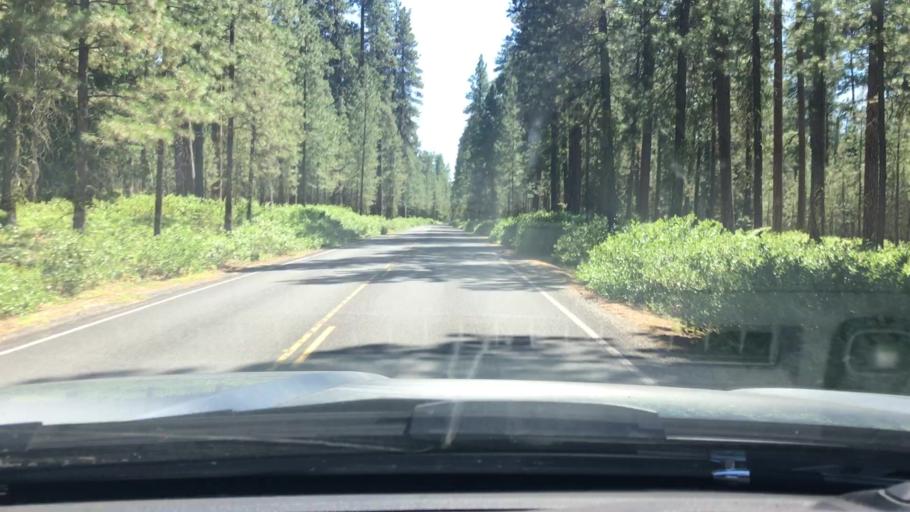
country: US
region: Oregon
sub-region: Deschutes County
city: Sisters
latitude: 44.4171
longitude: -121.6703
